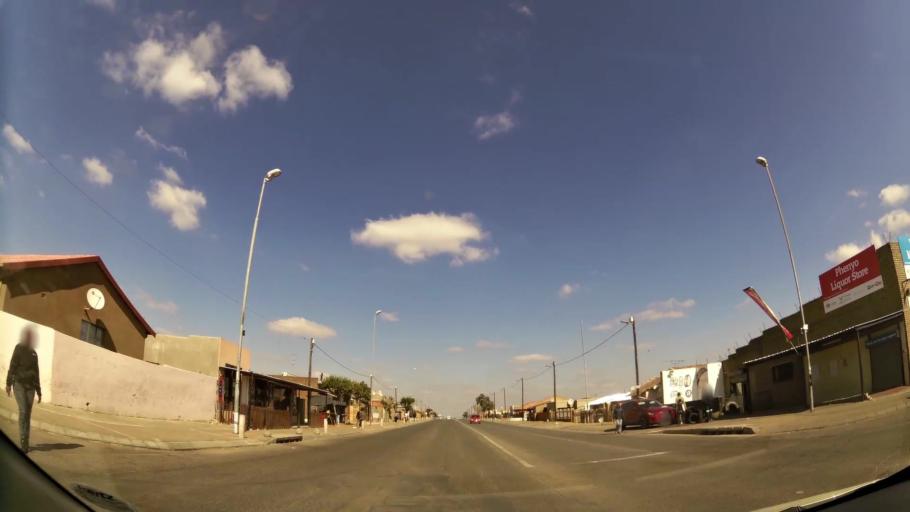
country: ZA
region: Gauteng
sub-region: West Rand District Municipality
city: Krugersdorp
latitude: -26.1550
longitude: 27.7852
